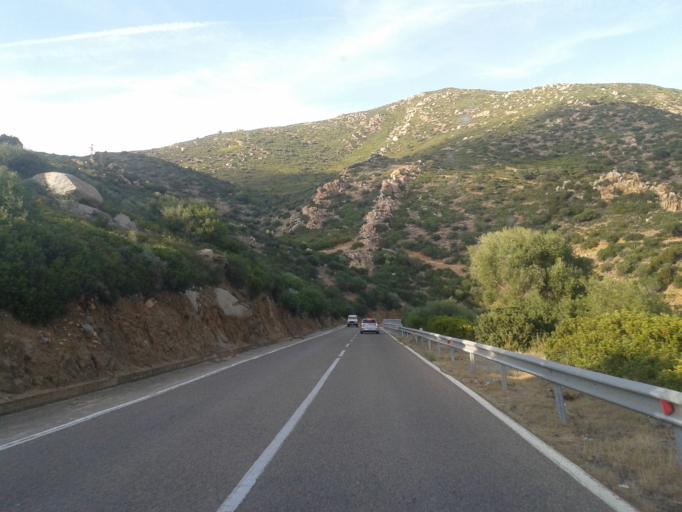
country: IT
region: Sardinia
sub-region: Provincia di Cagliari
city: Quartu Sant'Elena
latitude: 39.1799
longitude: 9.3520
